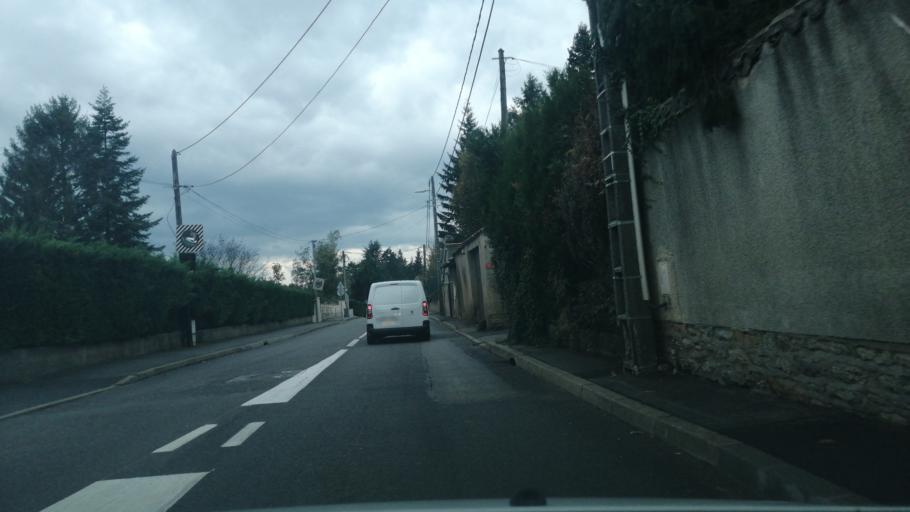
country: FR
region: Rhone-Alpes
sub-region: Departement du Rhone
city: Limonest
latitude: 45.8272
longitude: 4.7677
